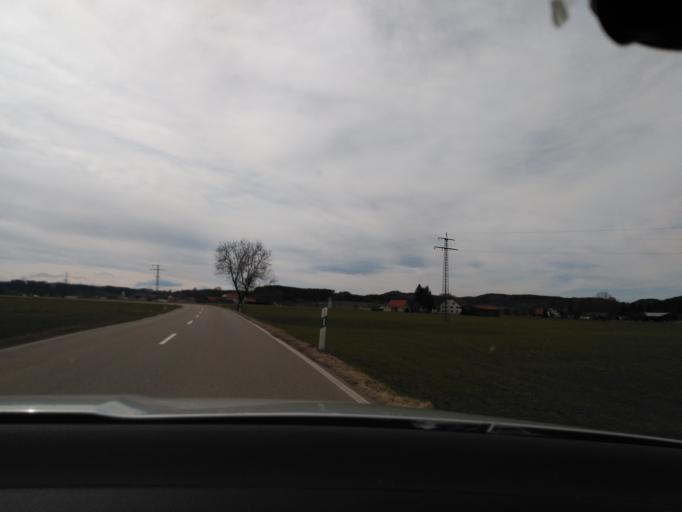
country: DE
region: Baden-Wuerttemberg
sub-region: Tuebingen Region
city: Aitrach
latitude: 47.9120
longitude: 10.0935
